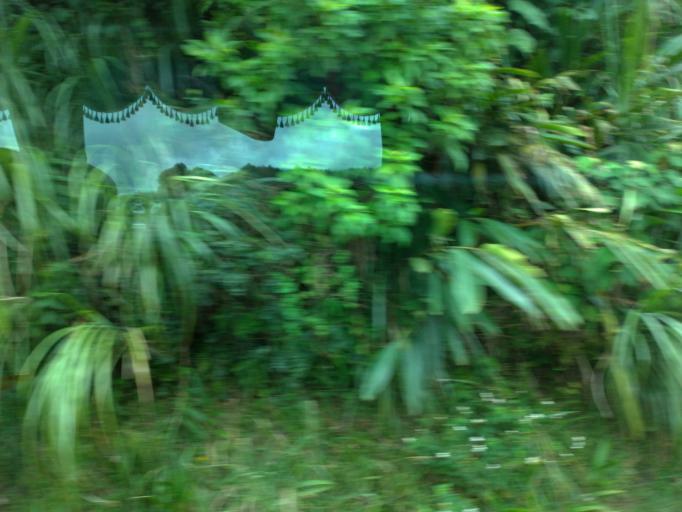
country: TW
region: Taiwan
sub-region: Keelung
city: Keelung
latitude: 25.1007
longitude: 121.7466
